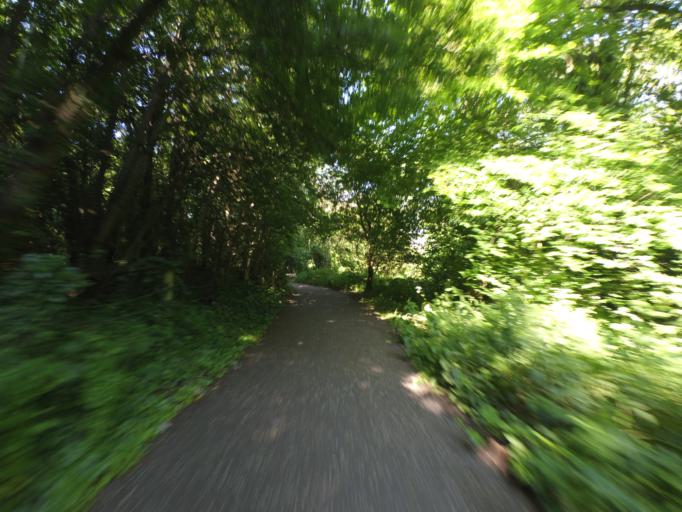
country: GB
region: Scotland
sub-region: East Lothian
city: Musselburgh
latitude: 55.9422
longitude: -3.0945
